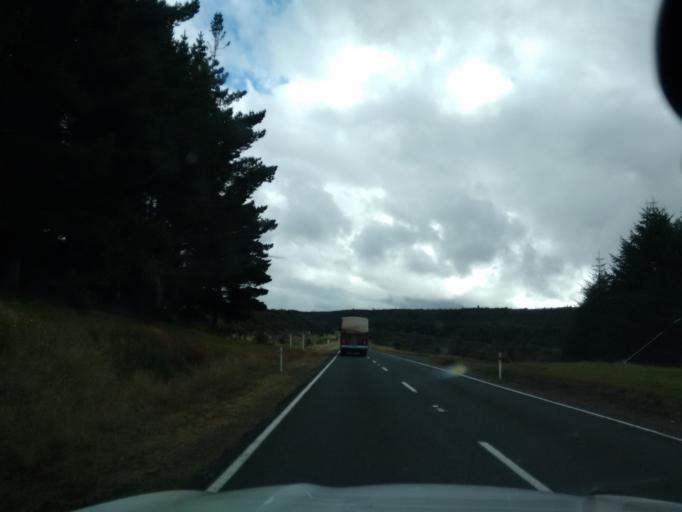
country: NZ
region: Waikato
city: Turangi
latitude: -39.0497
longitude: 175.5938
